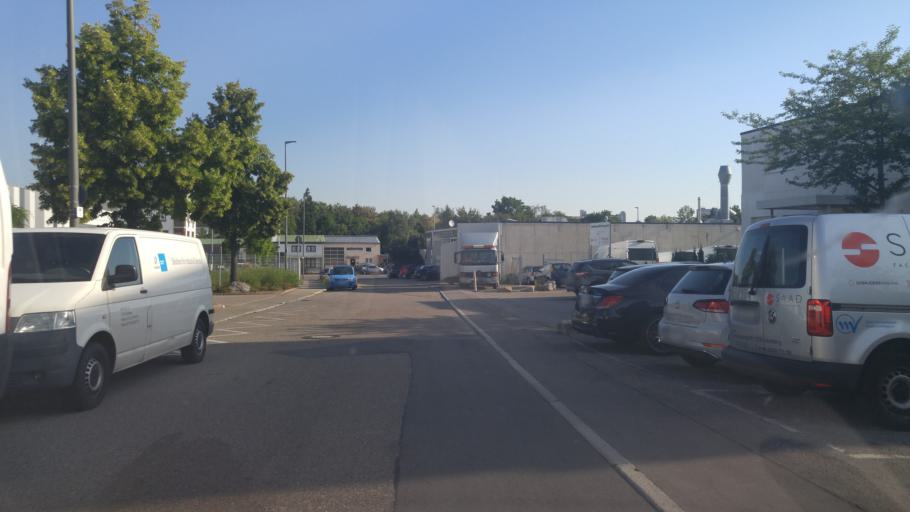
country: DE
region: Baden-Wuerttemberg
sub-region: Regierungsbezirk Stuttgart
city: Leonberg
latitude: 48.7856
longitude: 9.0018
